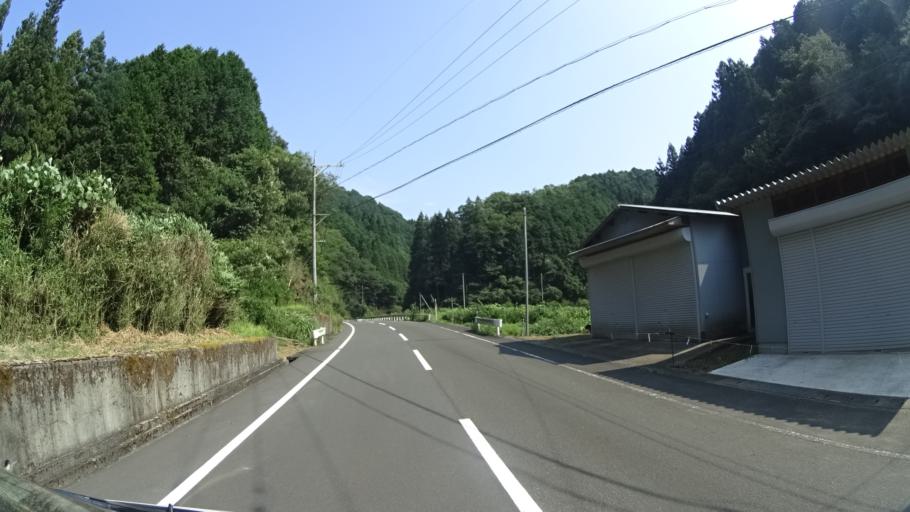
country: JP
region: Kyoto
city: Maizuru
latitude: 35.4162
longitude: 135.2291
